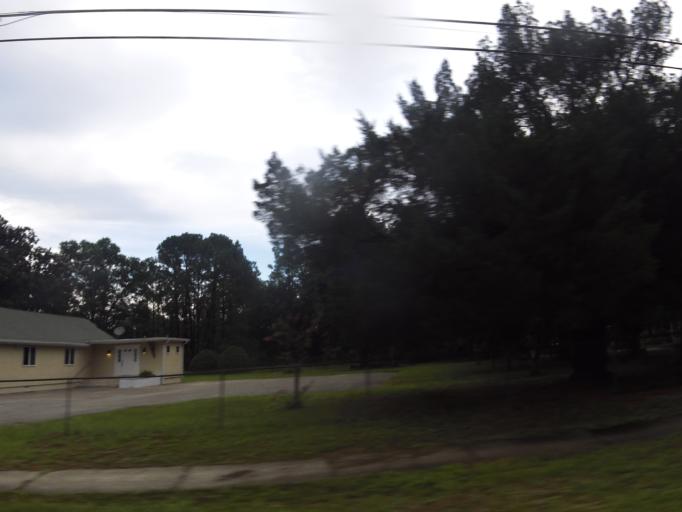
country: US
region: Florida
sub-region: Duval County
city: Jacksonville
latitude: 30.3178
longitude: -81.5416
